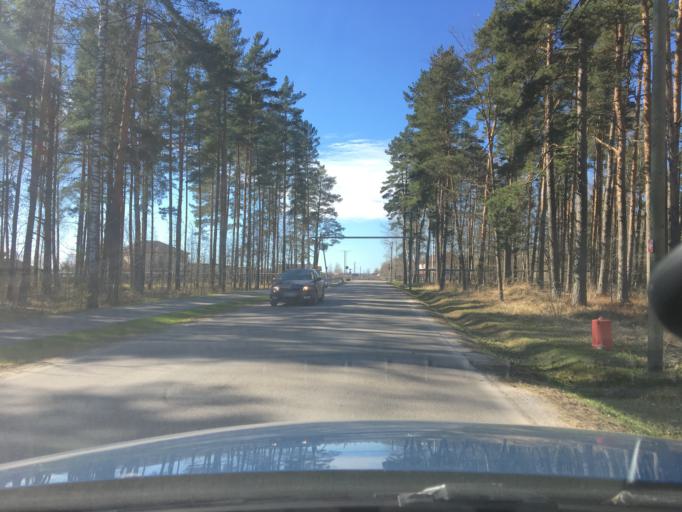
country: LV
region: Salaspils
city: Salaspils
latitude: 56.8715
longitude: 24.3424
